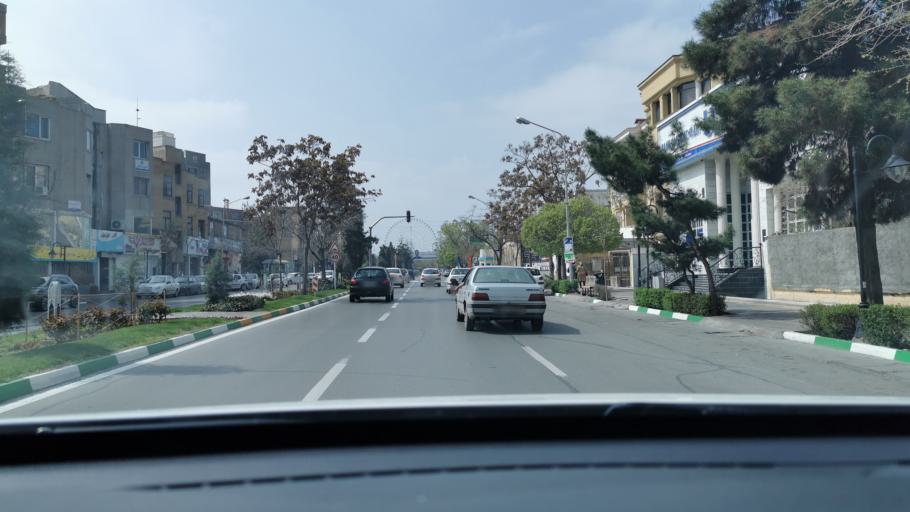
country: IR
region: Razavi Khorasan
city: Mashhad
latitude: 36.3186
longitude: 59.5456
